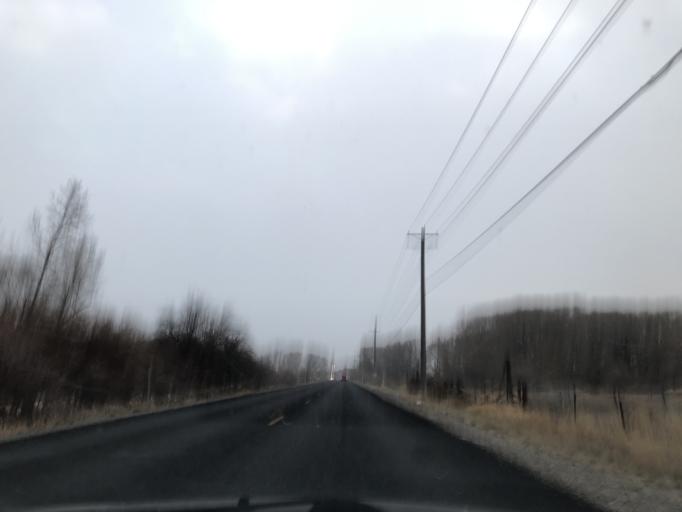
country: US
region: Utah
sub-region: Cache County
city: Logan
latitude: 41.7099
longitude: -111.8530
